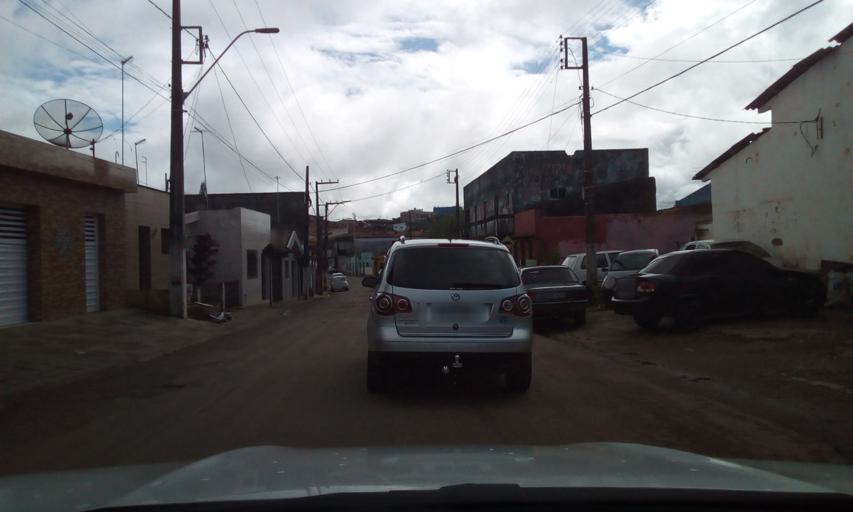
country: BR
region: Paraiba
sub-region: Areia
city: Areia
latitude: -6.9713
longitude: -35.6954
